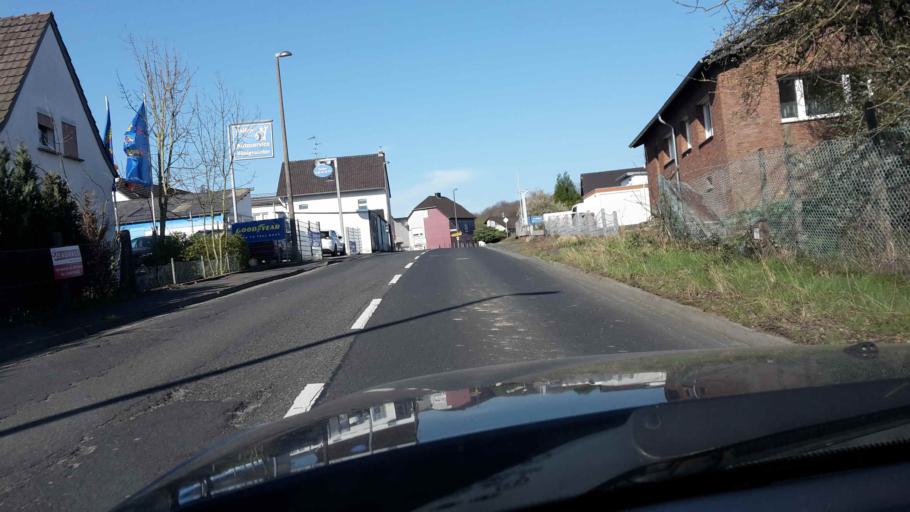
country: DE
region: North Rhine-Westphalia
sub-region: Regierungsbezirk Koln
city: Hennef
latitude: 50.7121
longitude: 7.3141
